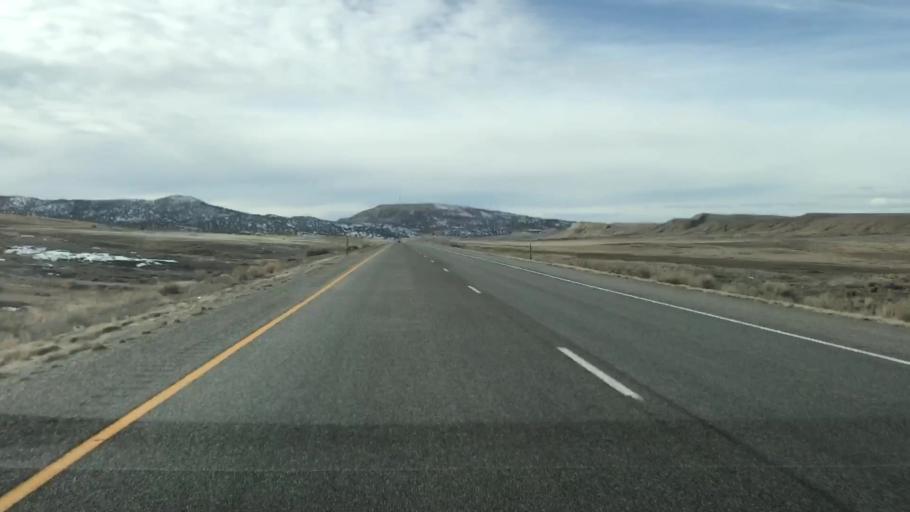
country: US
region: Colorado
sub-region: Mesa County
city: Loma
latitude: 39.2283
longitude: -108.9242
